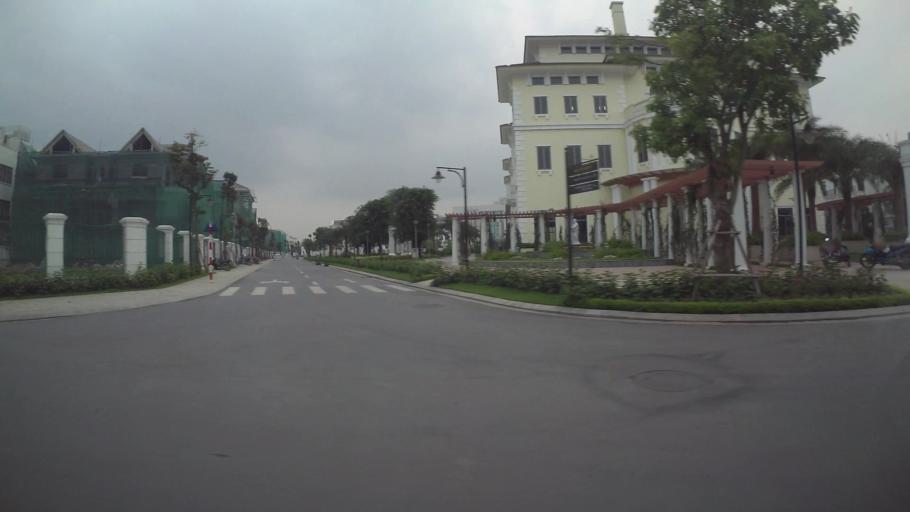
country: VN
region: Ha Noi
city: Trau Quy
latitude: 21.0465
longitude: 105.9056
